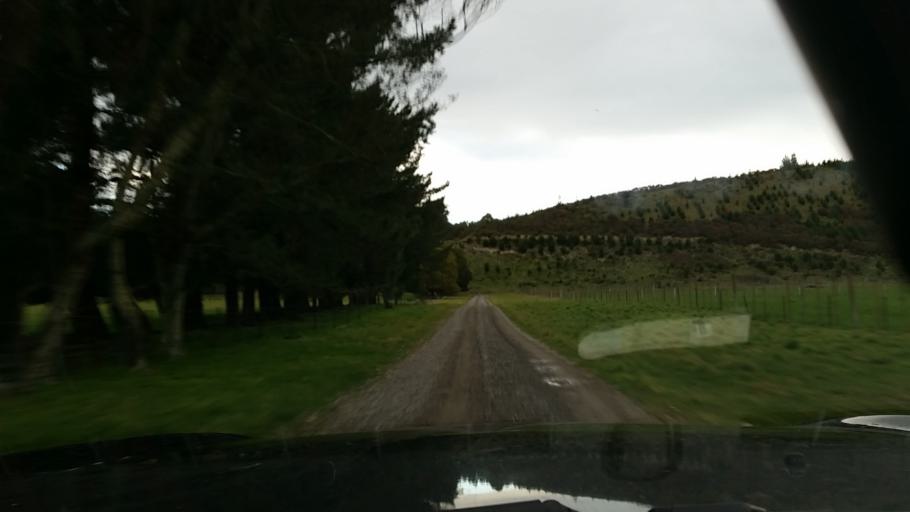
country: NZ
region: Marlborough
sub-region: Marlborough District
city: Blenheim
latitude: -41.5428
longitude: 173.6072
